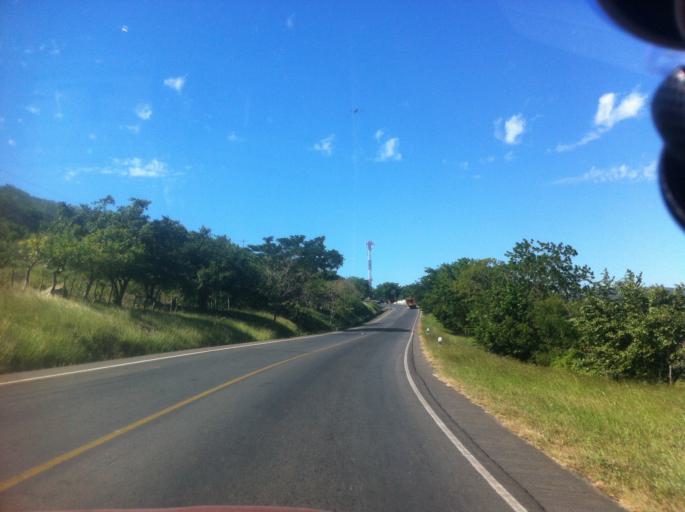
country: NI
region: Boaco
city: Teustepe
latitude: 12.3523
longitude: -85.9161
